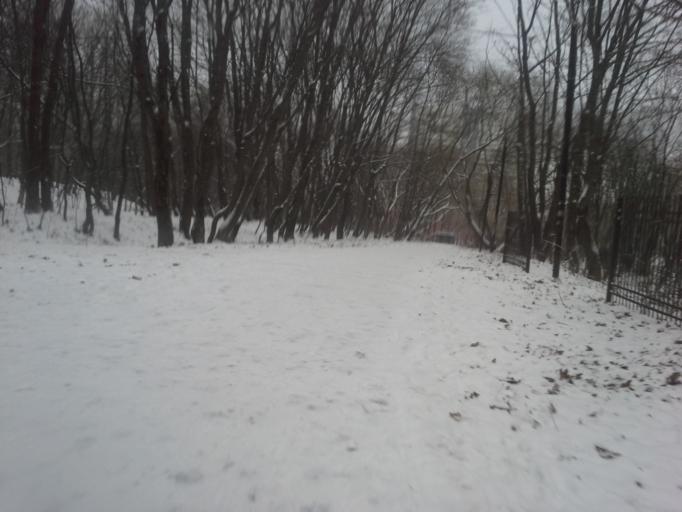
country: RU
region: Moscow
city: Yasenevo
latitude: 55.5989
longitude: 37.5477
